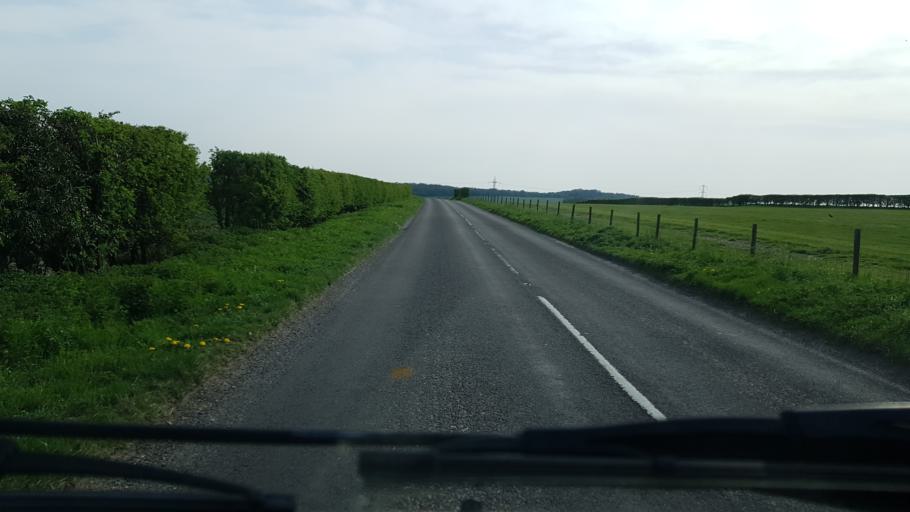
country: GB
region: England
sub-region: Hampshire
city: Kingsclere
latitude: 51.3027
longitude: -1.2638
